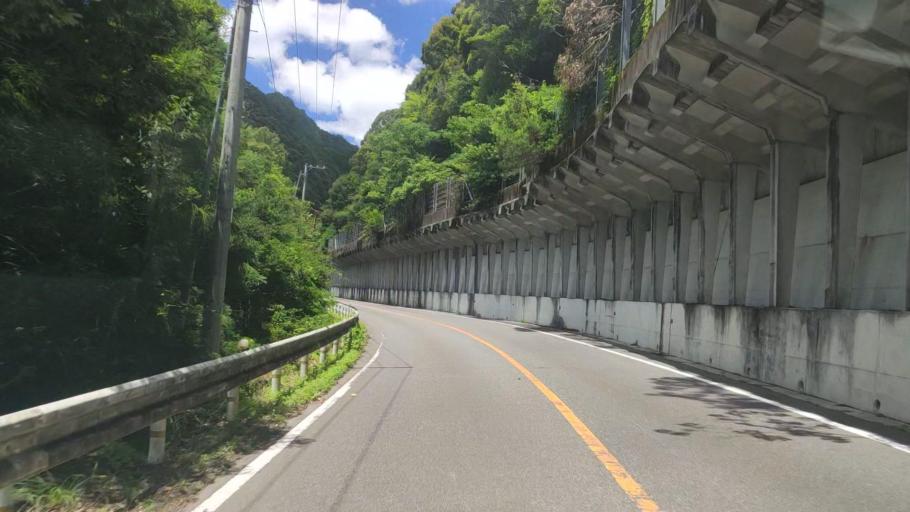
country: JP
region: Mie
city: Owase
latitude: 33.9997
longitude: 136.0103
